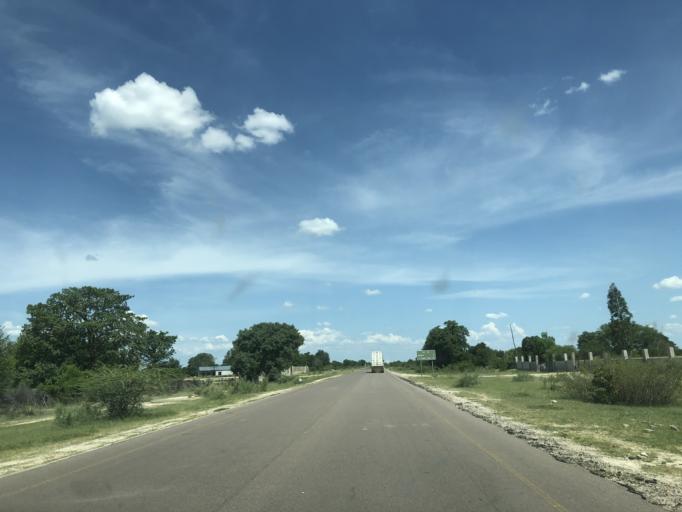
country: AO
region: Cunene
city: Ondjiva
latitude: -17.0017
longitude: 15.6390
